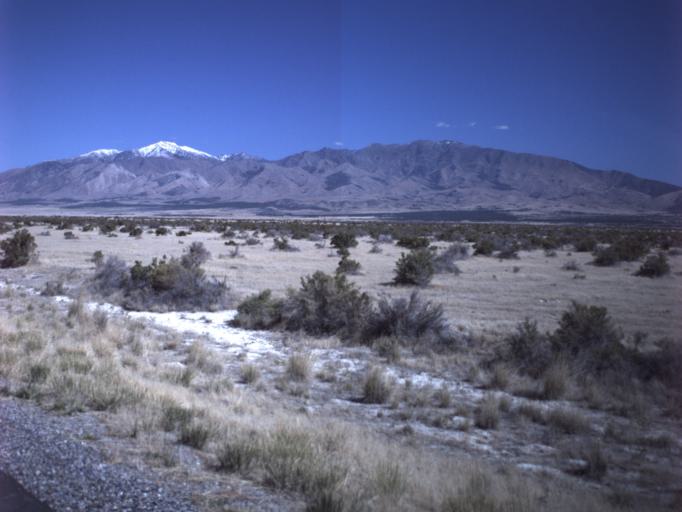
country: US
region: Utah
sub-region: Tooele County
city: Grantsville
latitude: 40.2655
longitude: -112.7410
